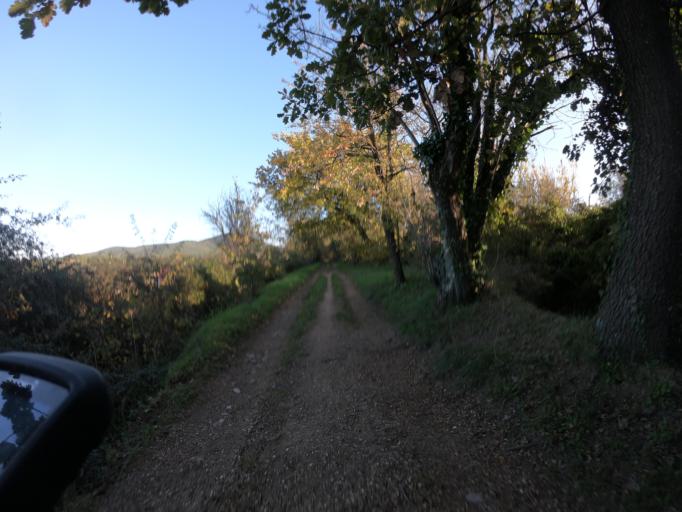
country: FR
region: Provence-Alpes-Cote d'Azur
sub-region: Departement du Var
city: Le Pradet
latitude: 43.1116
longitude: 6.0419
